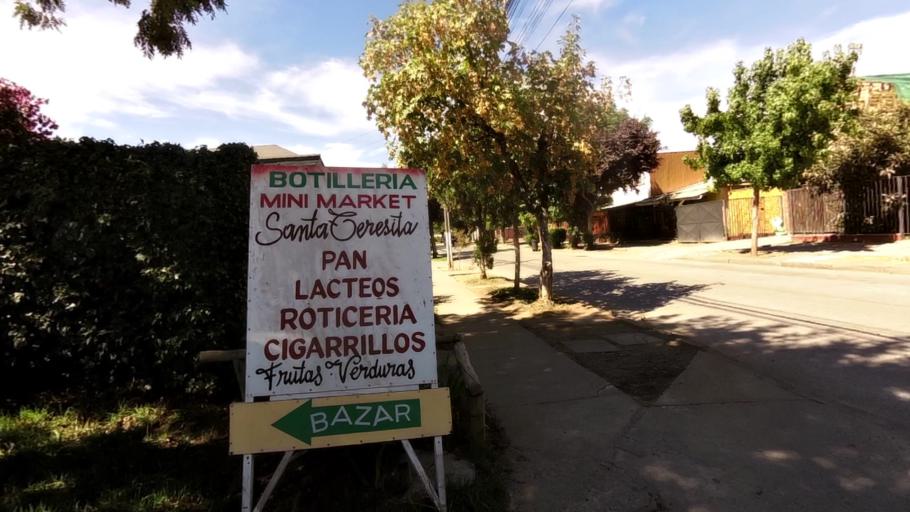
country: CL
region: O'Higgins
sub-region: Provincia de Cachapoal
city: Graneros
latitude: -33.9714
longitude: -70.7095
